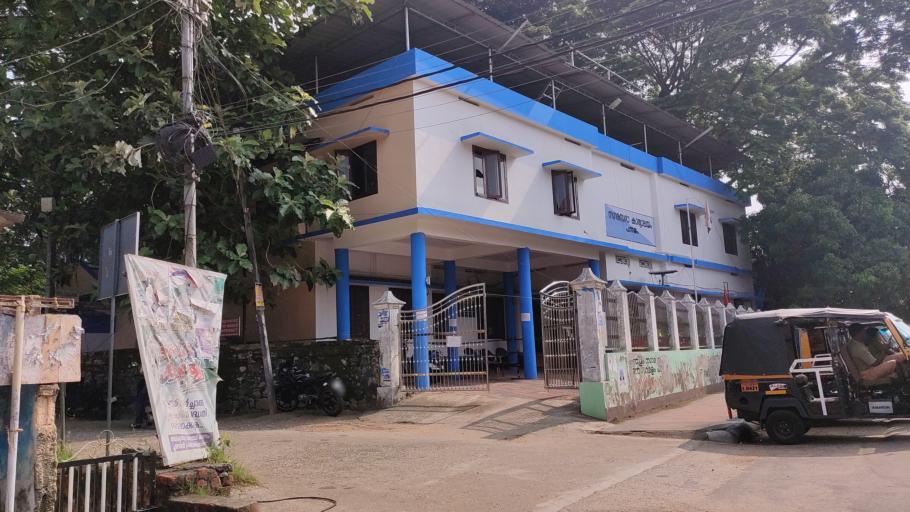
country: IN
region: Kerala
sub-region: Pattanamtitta
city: Adur
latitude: 9.2244
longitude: 76.6773
